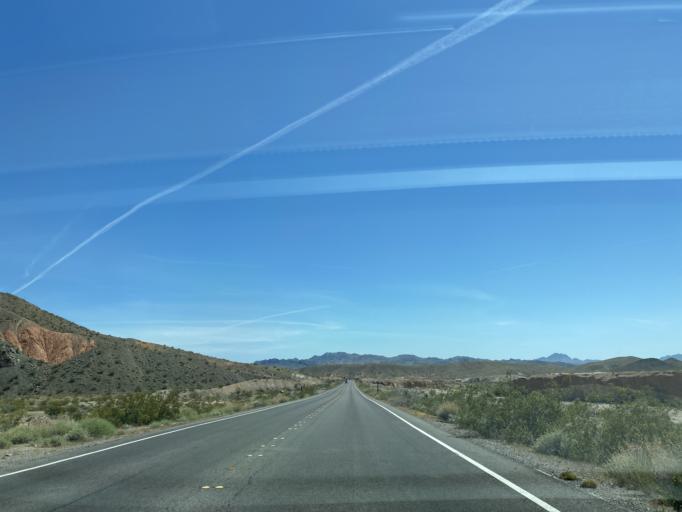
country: US
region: Nevada
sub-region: Clark County
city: Henderson
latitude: 36.1736
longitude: -114.9128
